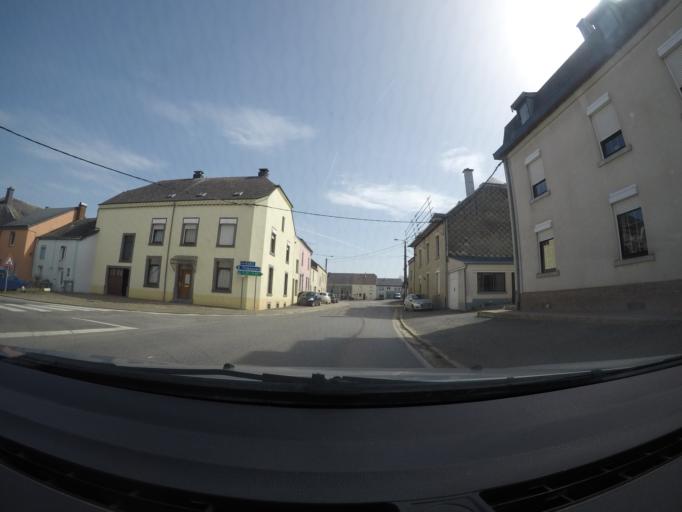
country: BE
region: Wallonia
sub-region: Province du Luxembourg
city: Habay-la-Vieille
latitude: 49.7187
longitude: 5.5844
